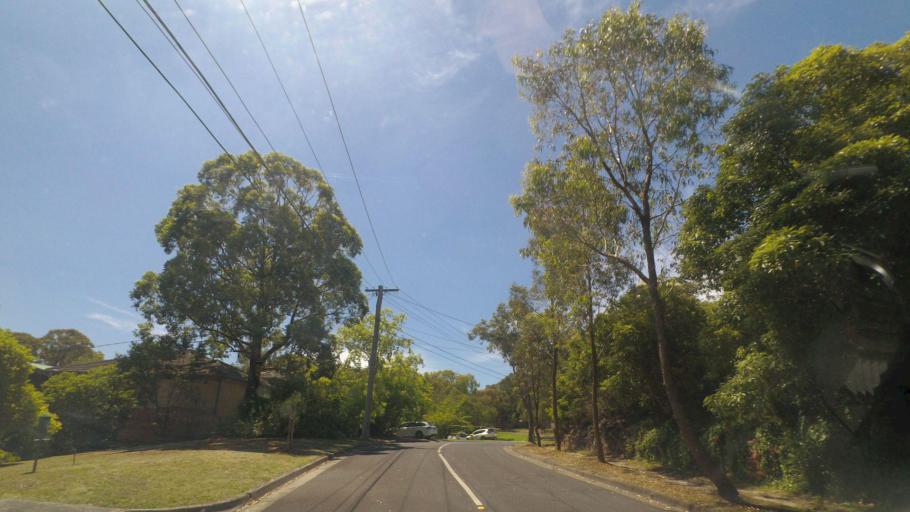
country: AU
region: Victoria
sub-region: Manningham
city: Park Orchards
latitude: -37.7998
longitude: 145.2255
